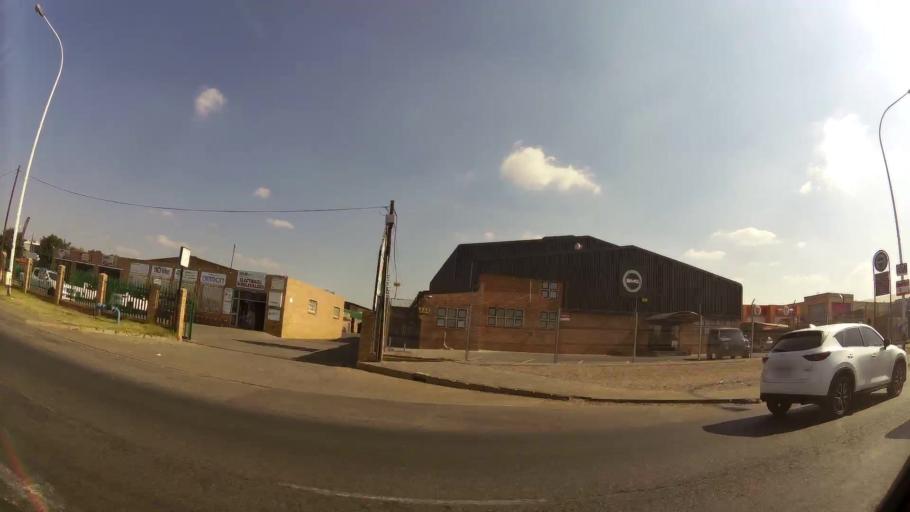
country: ZA
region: Gauteng
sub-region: Ekurhuleni Metropolitan Municipality
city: Boksburg
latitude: -26.1986
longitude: 28.2833
